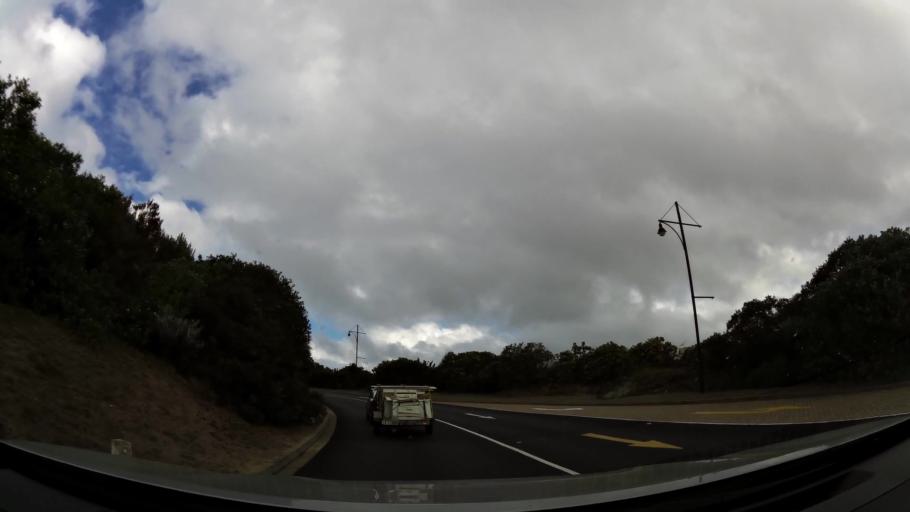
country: ZA
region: Western Cape
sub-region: Eden District Municipality
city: Knysna
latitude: -34.0700
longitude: 23.0873
